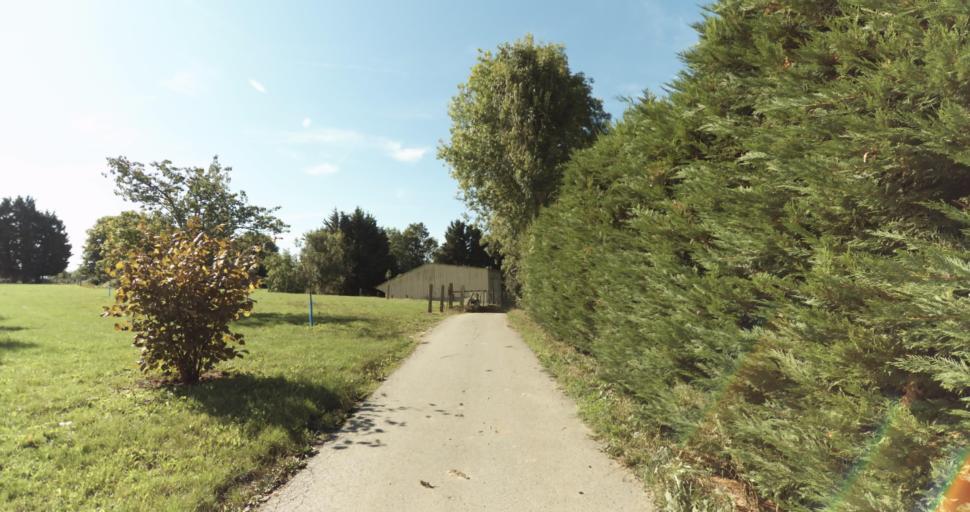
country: FR
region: Lower Normandy
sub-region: Departement de l'Orne
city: Gace
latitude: 48.8021
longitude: 0.2296
